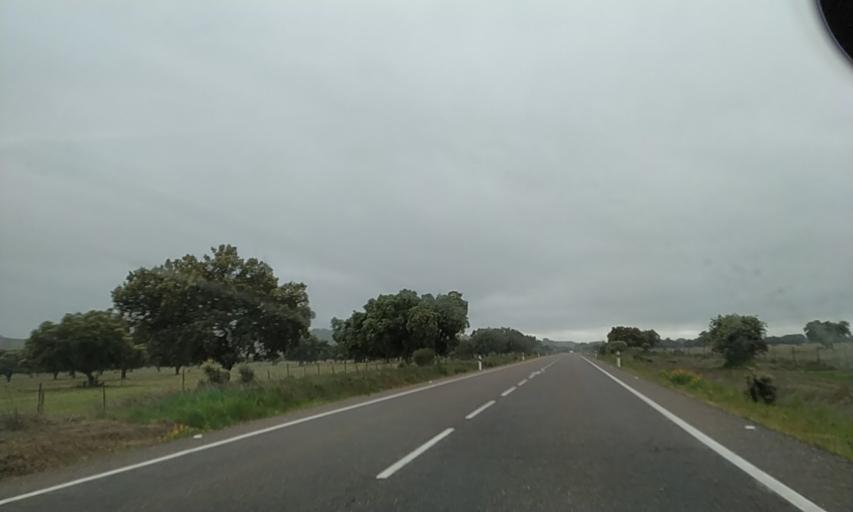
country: ES
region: Extremadura
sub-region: Provincia de Badajoz
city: La Roca de la Sierra
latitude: 39.0946
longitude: -6.7154
